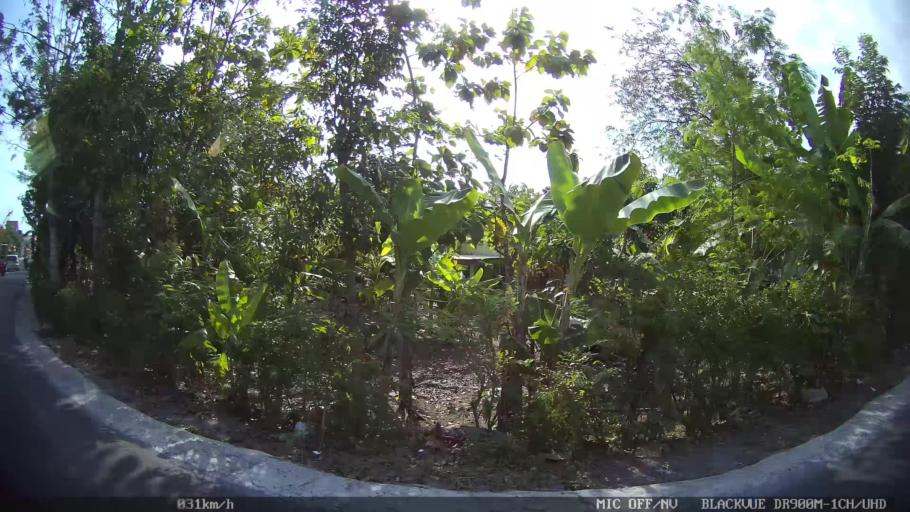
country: ID
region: Daerah Istimewa Yogyakarta
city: Kasihan
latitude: -7.8352
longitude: 110.3231
